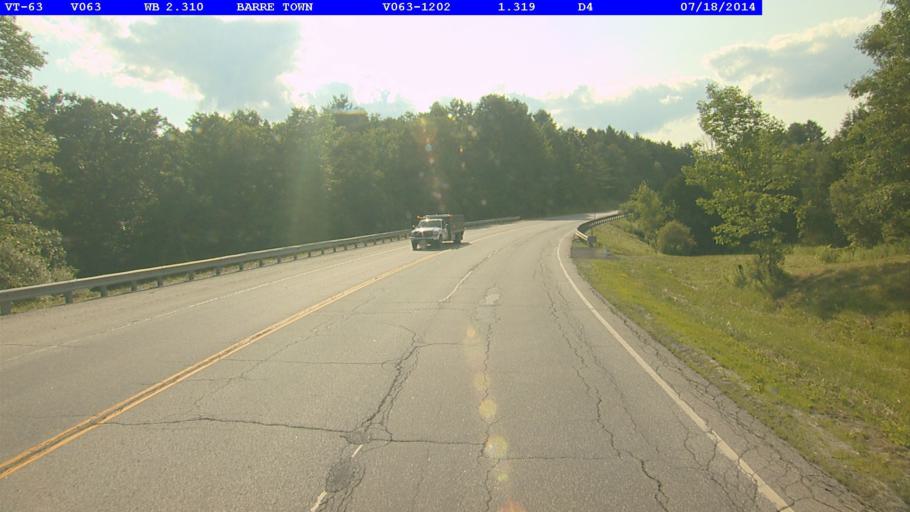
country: US
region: Vermont
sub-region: Washington County
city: South Barre
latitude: 44.1629
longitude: -72.5334
